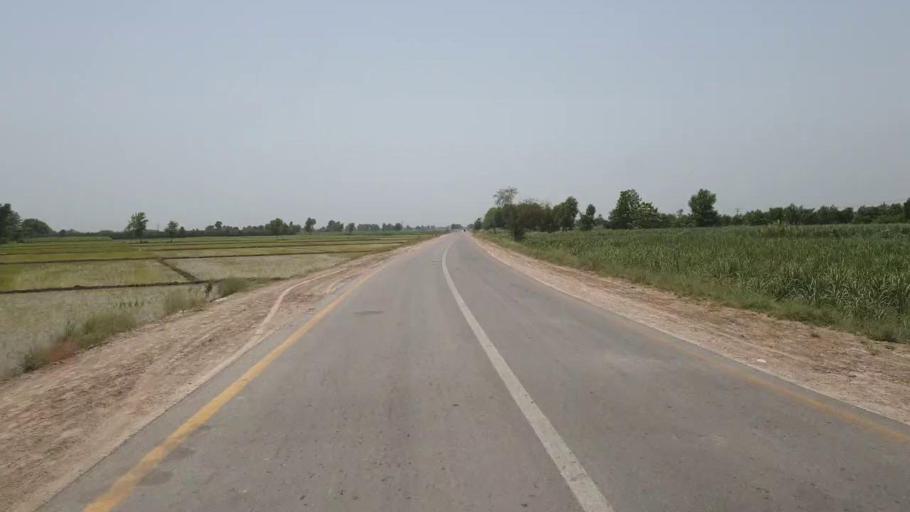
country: PK
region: Sindh
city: Moro
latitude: 26.6029
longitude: 68.0576
